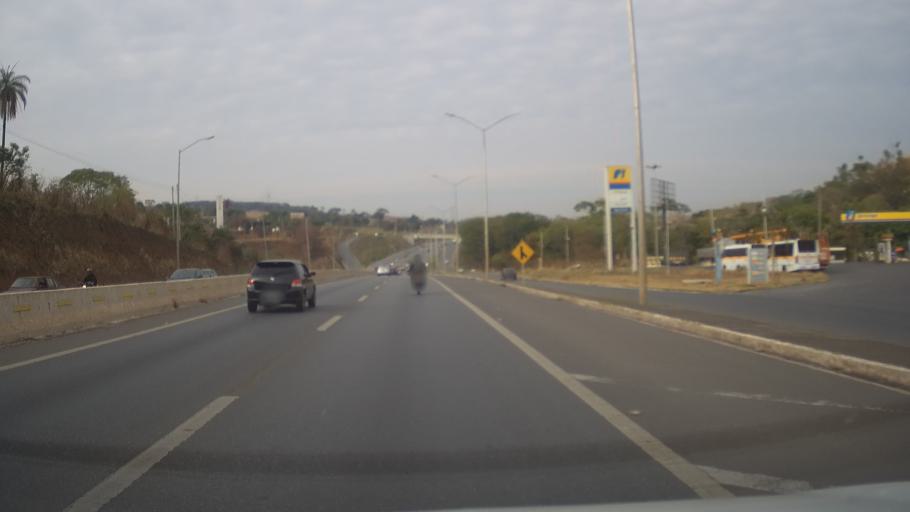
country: BR
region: Minas Gerais
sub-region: Vespasiano
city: Vespasiano
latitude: -19.7174
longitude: -43.9293
